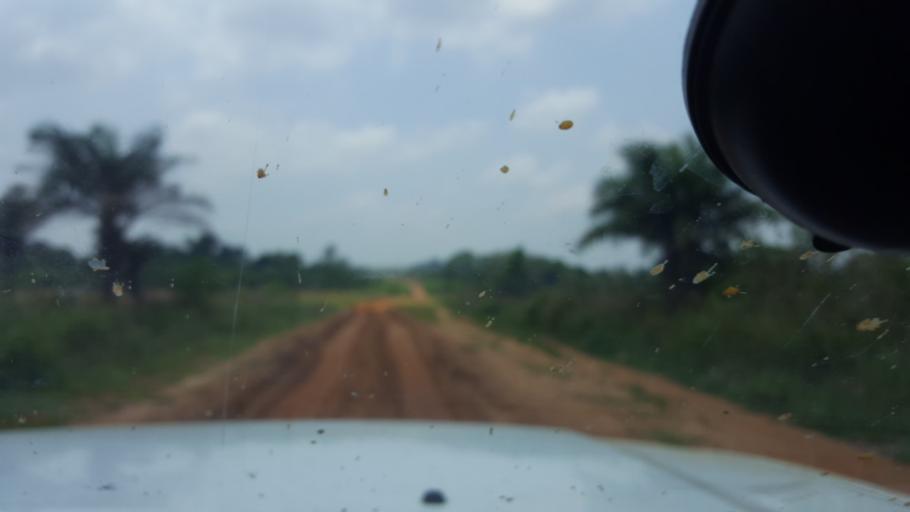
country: CD
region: Bandundu
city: Mushie
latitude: -3.7466
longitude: 16.6569
